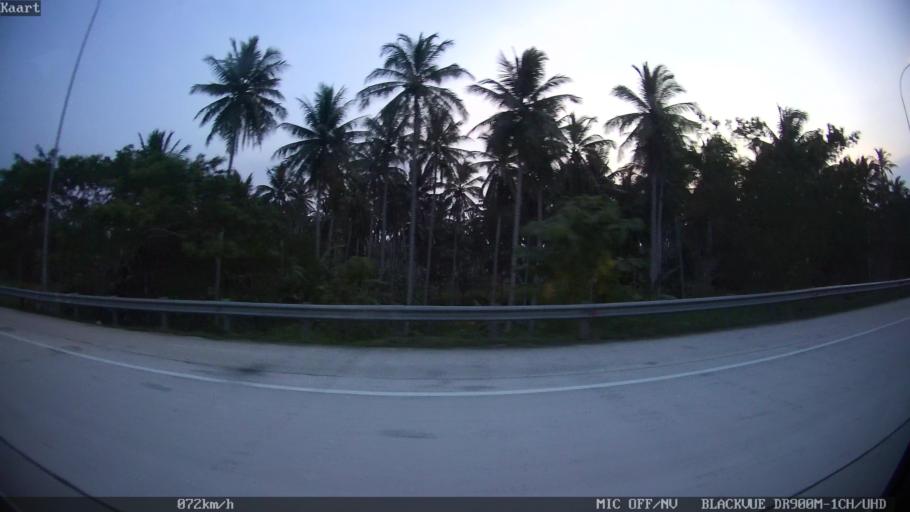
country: ID
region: Lampung
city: Kalianda
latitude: -5.6558
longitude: 105.5875
